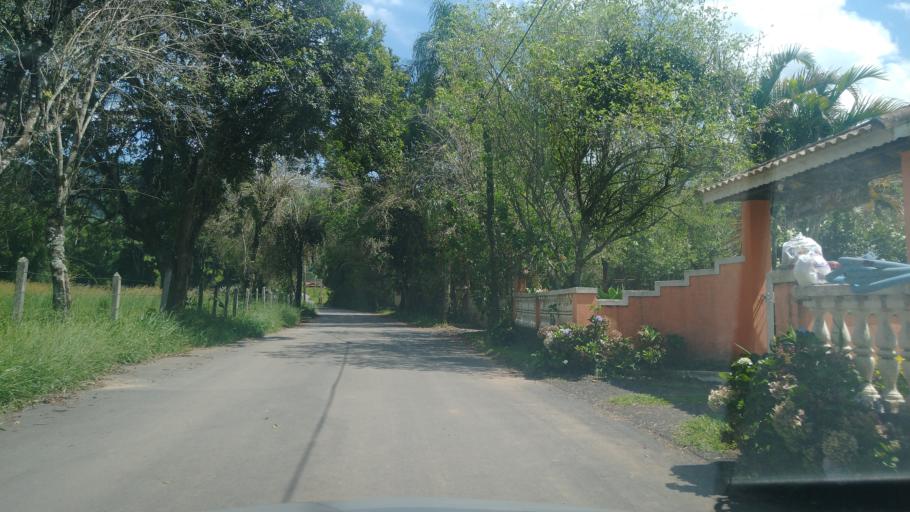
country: BR
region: Minas Gerais
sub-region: Extrema
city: Extrema
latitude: -22.7663
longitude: -46.2825
